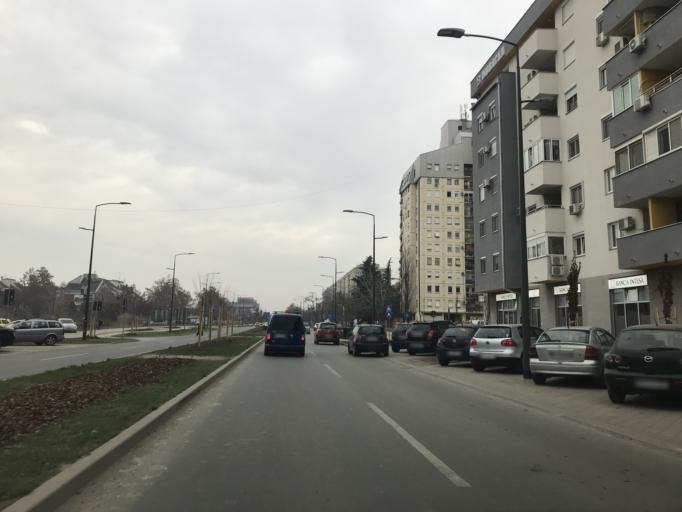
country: RS
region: Autonomna Pokrajina Vojvodina
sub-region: Juznobacki Okrug
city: Novi Sad
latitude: 45.2491
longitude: 19.7986
